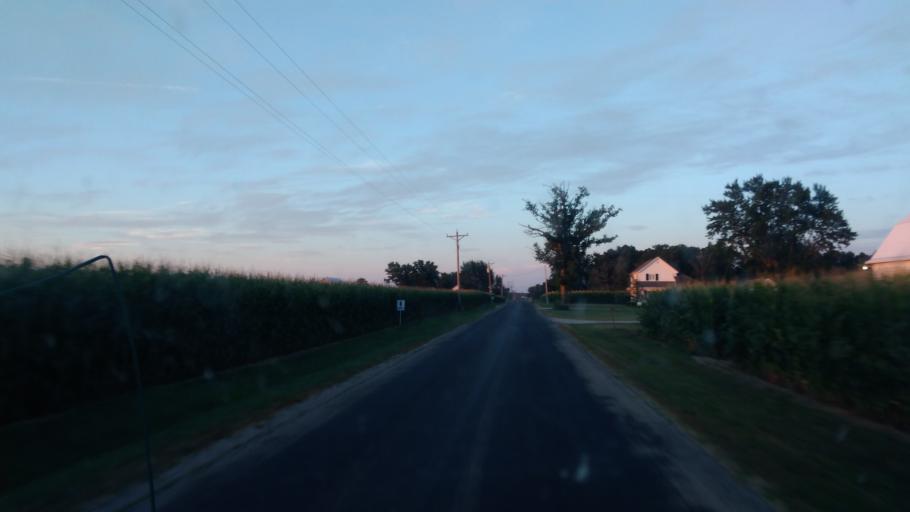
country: US
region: Indiana
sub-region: Wells County
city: Bluffton
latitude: 40.6757
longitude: -85.1073
